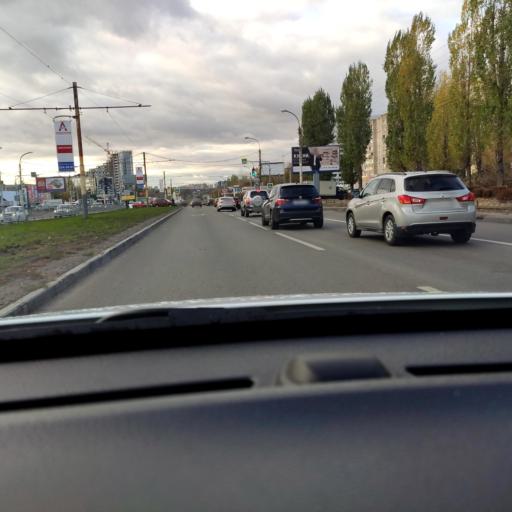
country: RU
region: Voronezj
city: Voronezh
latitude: 51.6870
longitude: 39.2604
